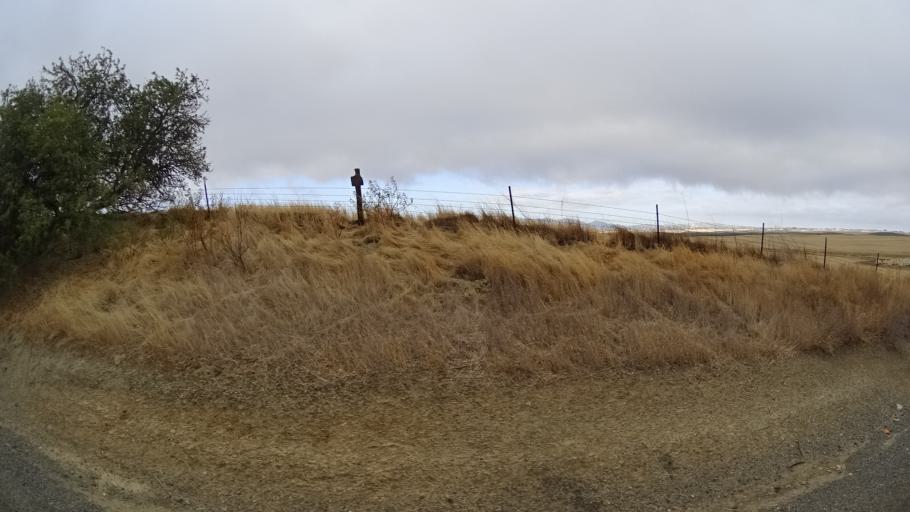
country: US
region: California
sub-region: Yolo County
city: Dunnigan
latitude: 38.8268
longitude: -122.0433
